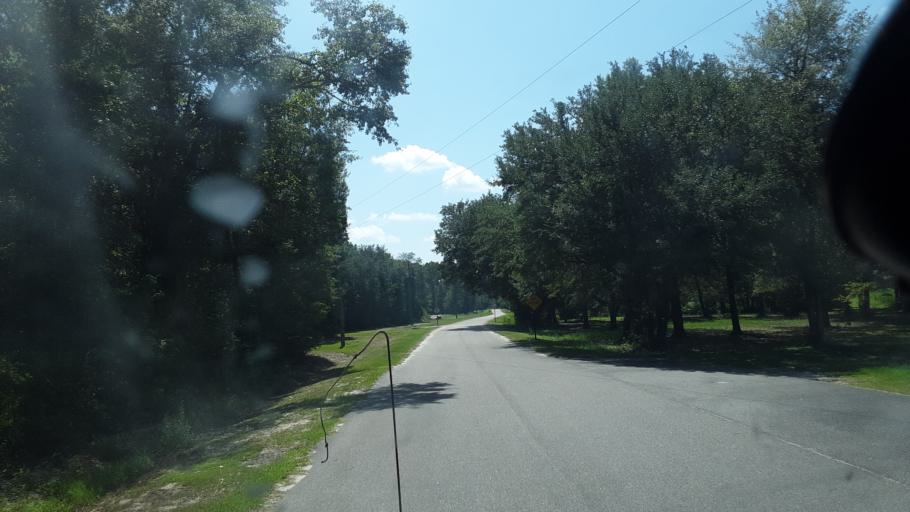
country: US
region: South Carolina
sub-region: Horry County
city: Forestbrook
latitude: 33.8415
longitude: -78.8627
